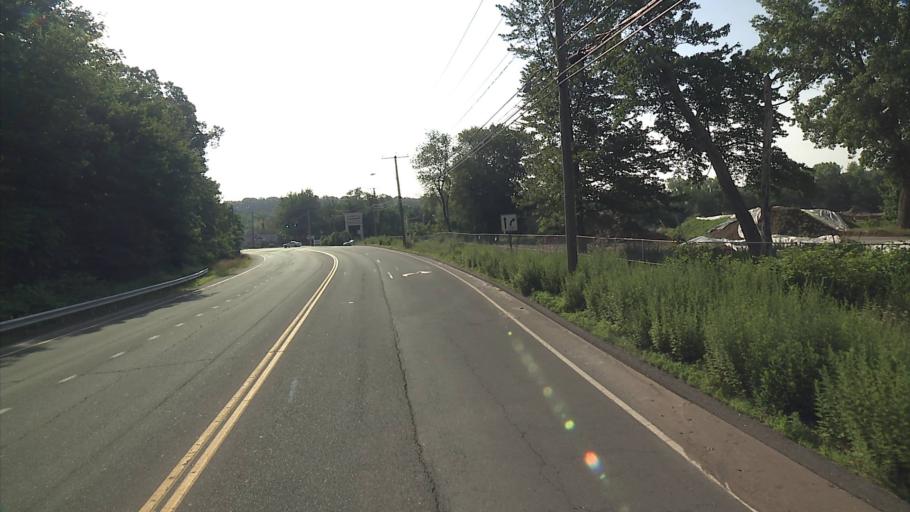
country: US
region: Connecticut
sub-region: New Haven County
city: Prospect
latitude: 41.5427
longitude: -72.9704
